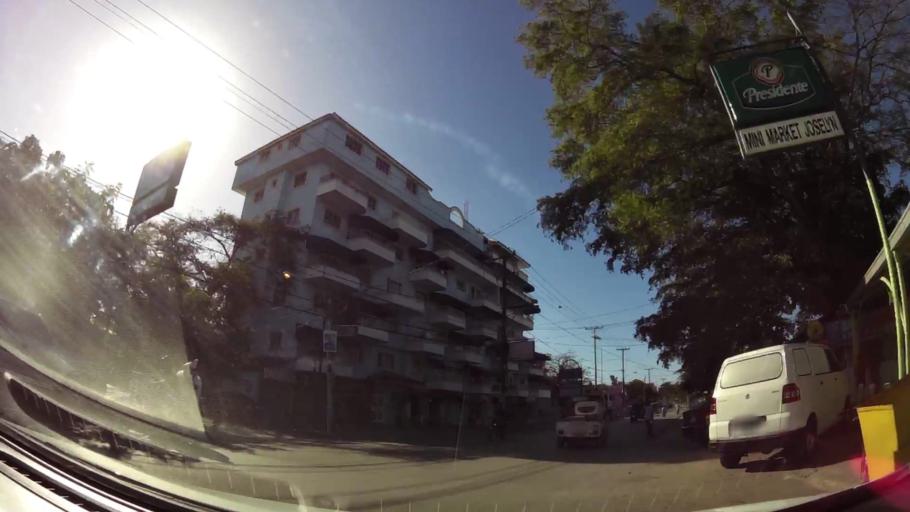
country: DO
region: Santo Domingo
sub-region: Santo Domingo
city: Boca Chica
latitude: 18.4537
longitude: -69.6057
